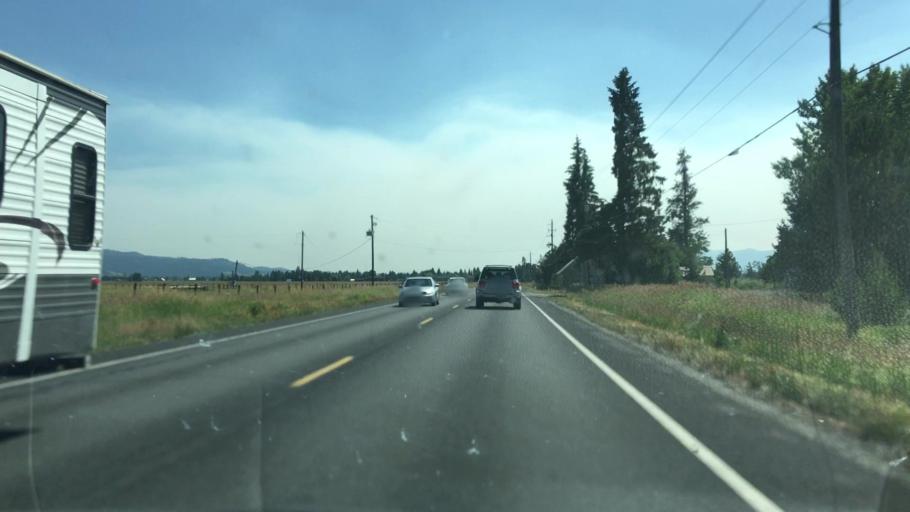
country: US
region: Idaho
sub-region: Valley County
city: McCall
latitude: 44.7469
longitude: -116.0783
